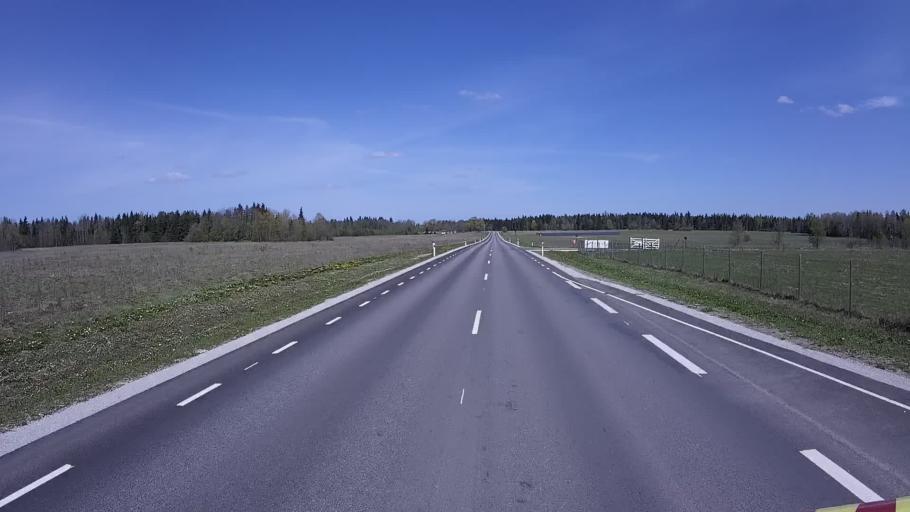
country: EE
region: Harju
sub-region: Paldiski linn
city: Paldiski
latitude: 59.1924
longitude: 24.0926
